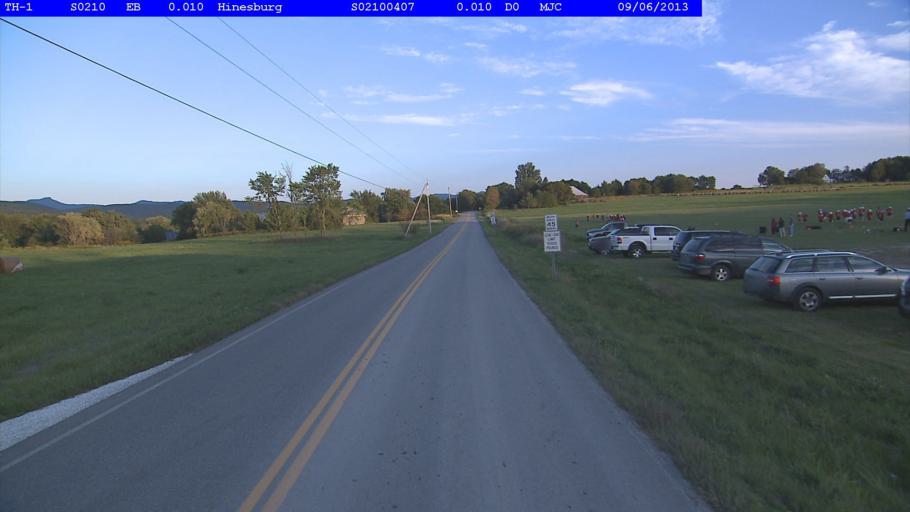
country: US
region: Vermont
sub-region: Chittenden County
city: Hinesburg
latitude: 44.3625
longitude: -73.1616
